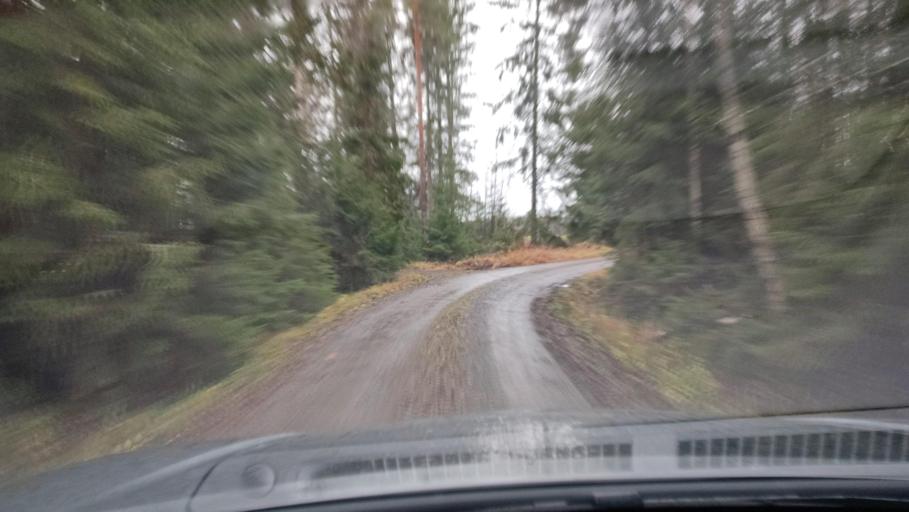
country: FI
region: Southern Ostrobothnia
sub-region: Suupohja
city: Karijoki
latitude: 62.2315
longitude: 21.5513
